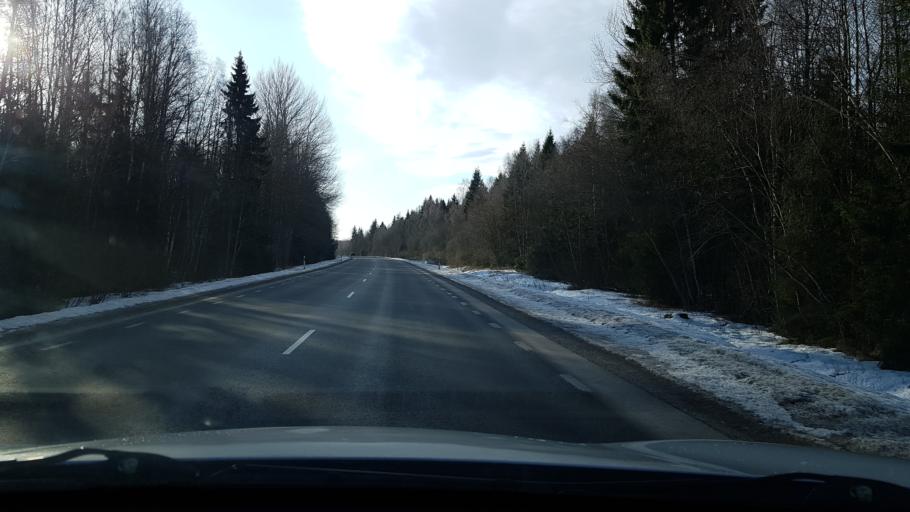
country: EE
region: Viljandimaa
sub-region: Vohma linn
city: Vohma
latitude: 58.5771
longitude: 25.5693
